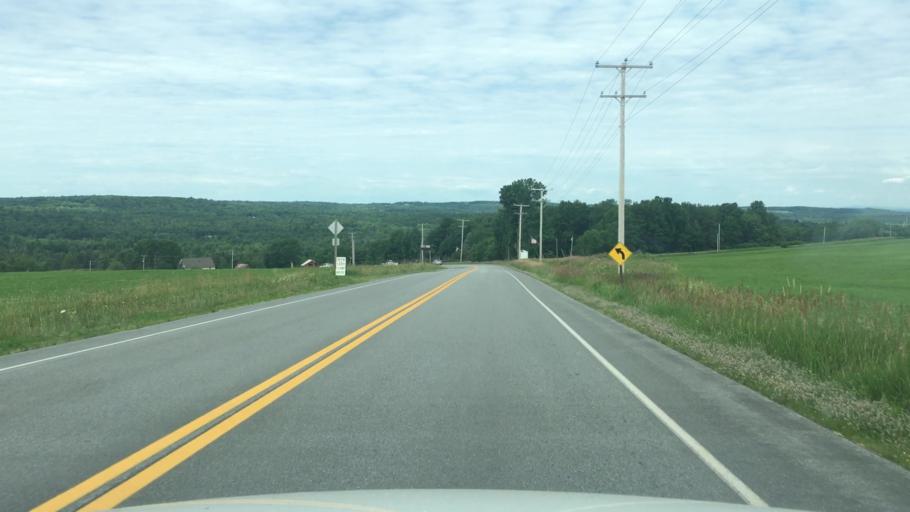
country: US
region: Maine
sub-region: Waldo County
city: Troy
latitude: 44.5334
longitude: -69.2721
